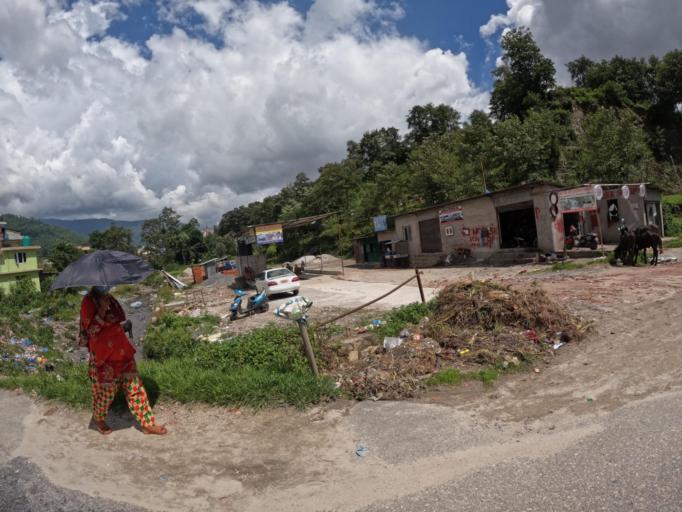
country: NP
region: Central Region
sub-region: Bagmati Zone
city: Kathmandu
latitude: 27.7714
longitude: 85.3297
